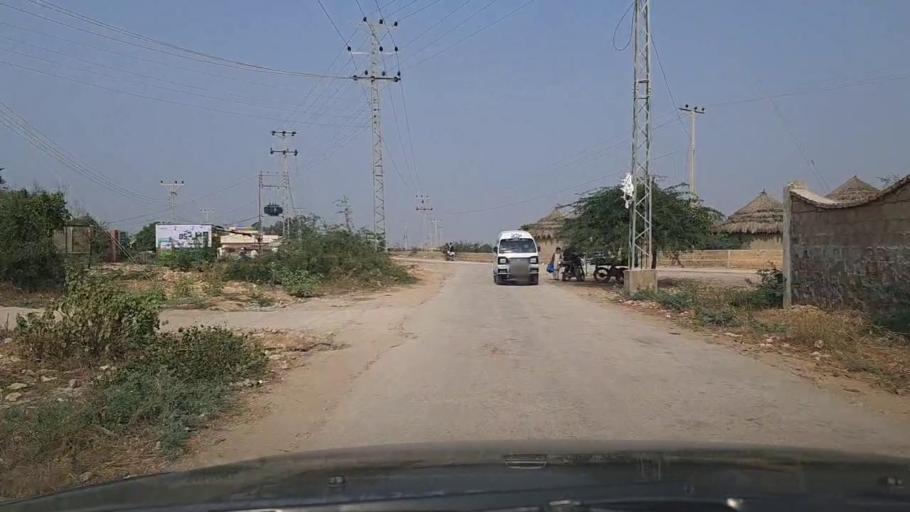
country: PK
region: Sindh
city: Thatta
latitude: 24.7517
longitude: 67.8970
